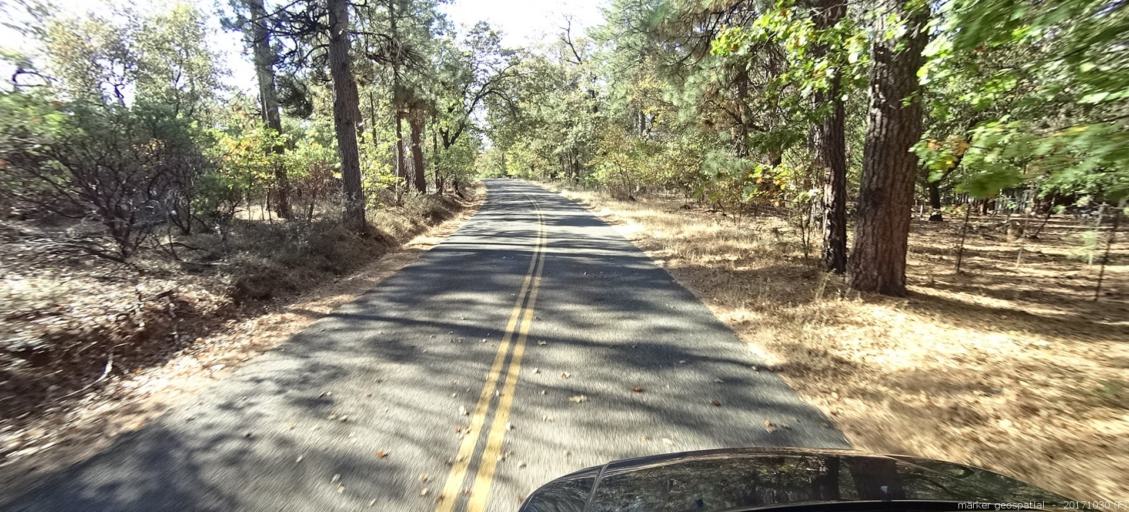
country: US
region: California
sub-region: Shasta County
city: Shingletown
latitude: 40.6111
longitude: -121.9520
